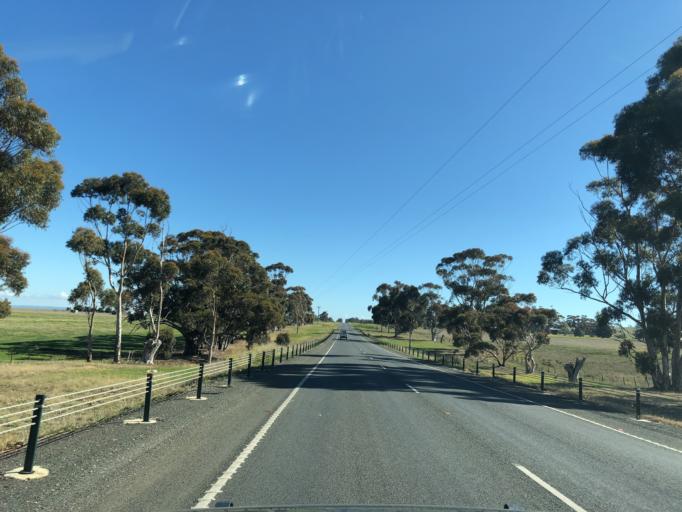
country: AU
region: Victoria
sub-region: Melton
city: Kurunjang
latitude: -37.6093
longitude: 144.5868
